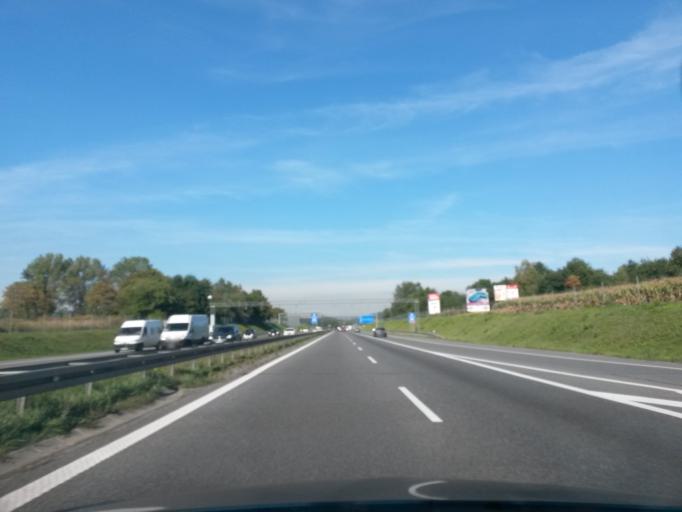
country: PL
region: Lesser Poland Voivodeship
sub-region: Powiat krakowski
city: Balice
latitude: 50.0756
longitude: 19.8095
